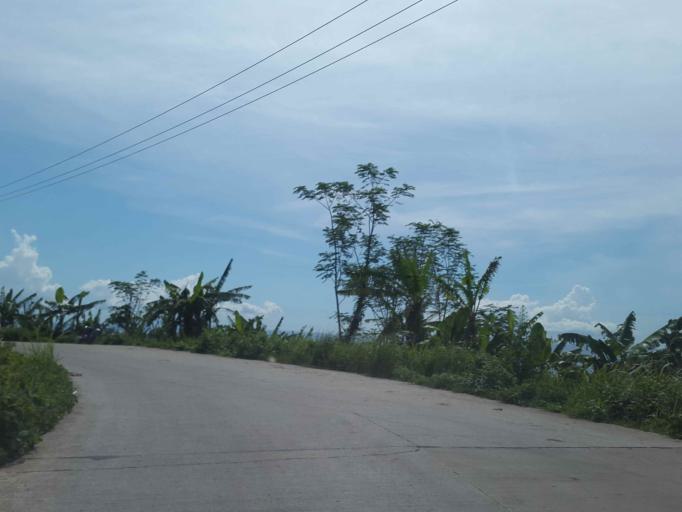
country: ID
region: Banten
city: Babakanbungur
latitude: -6.5191
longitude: 105.6313
